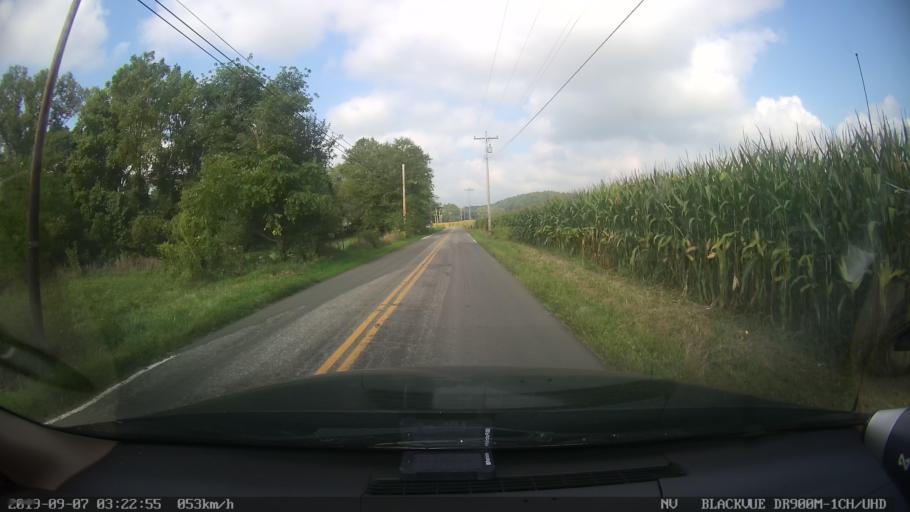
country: US
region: Ohio
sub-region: Licking County
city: Granville
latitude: 40.1191
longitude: -82.4642
